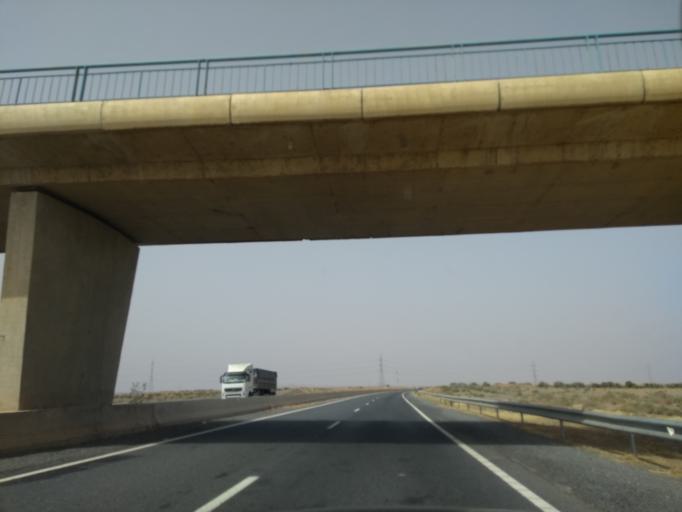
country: MA
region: Marrakech-Tensift-Al Haouz
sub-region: Marrakech
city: Marrakesh
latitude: 31.7589
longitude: -8.1856
